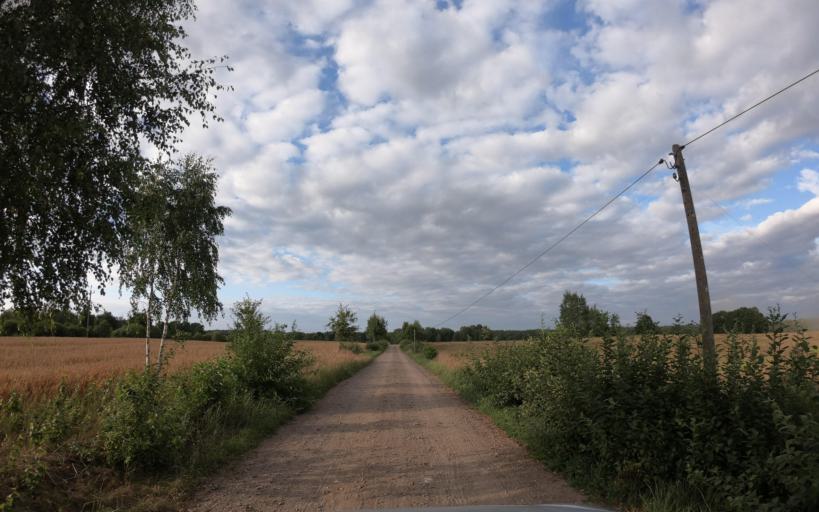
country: PL
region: West Pomeranian Voivodeship
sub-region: Powiat drawski
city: Czaplinek
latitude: 53.5297
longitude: 16.1546
